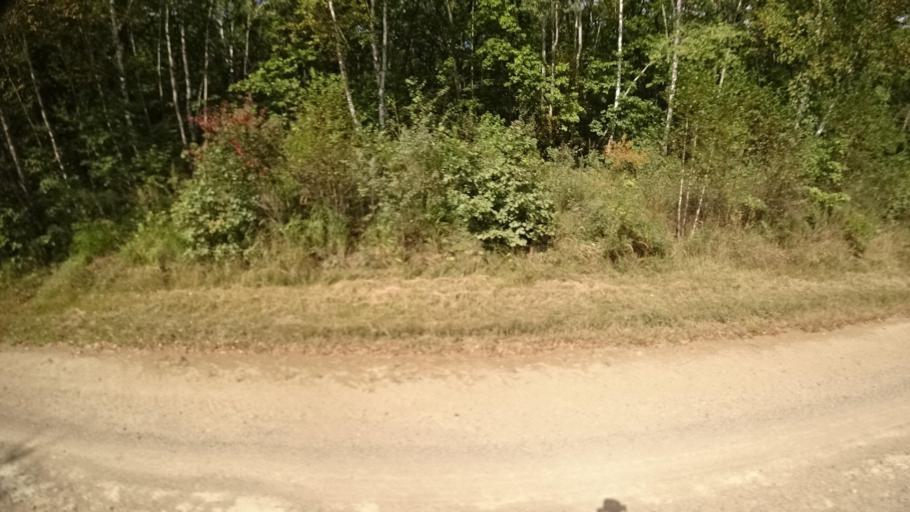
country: RU
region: Primorskiy
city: Yakovlevka
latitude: 44.6626
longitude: 133.6019
